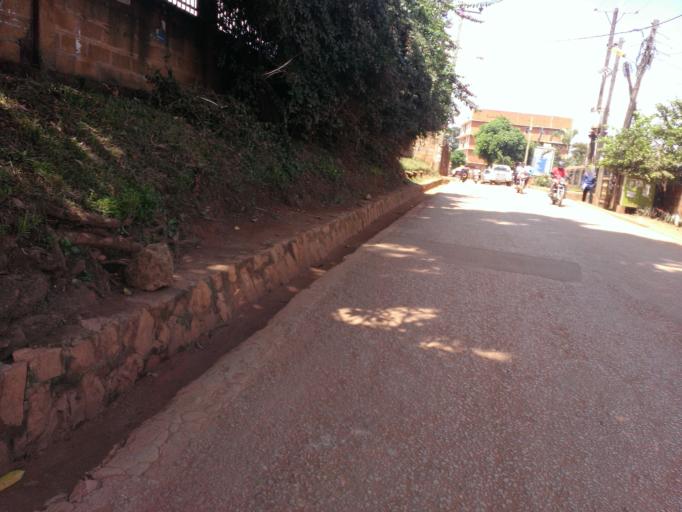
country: UG
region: Central Region
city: Kampala Central Division
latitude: 0.3259
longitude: 32.5663
